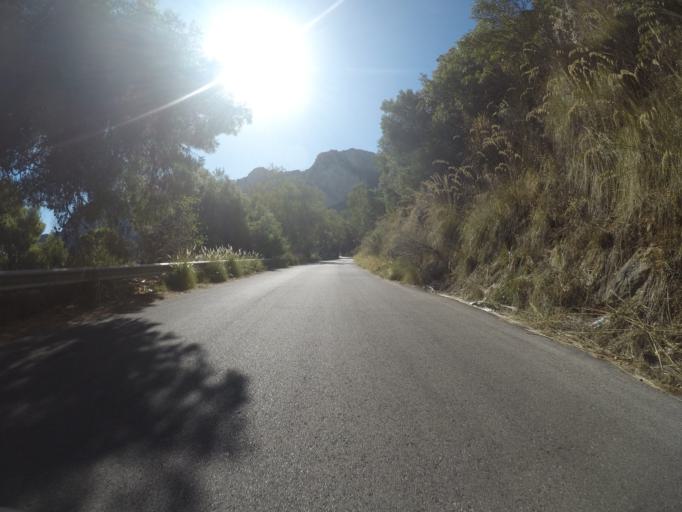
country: IT
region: Sicily
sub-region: Palermo
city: Palermo
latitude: 38.1911
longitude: 13.3394
